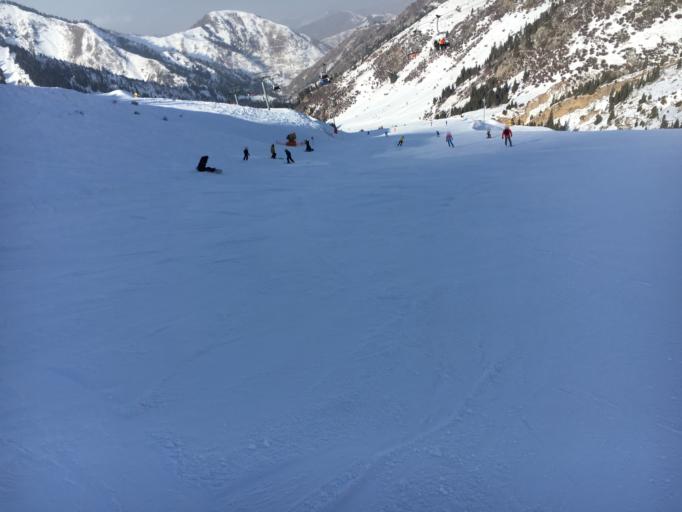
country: KZ
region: Almaty Qalasy
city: Almaty
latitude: 43.1208
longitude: 77.0957
